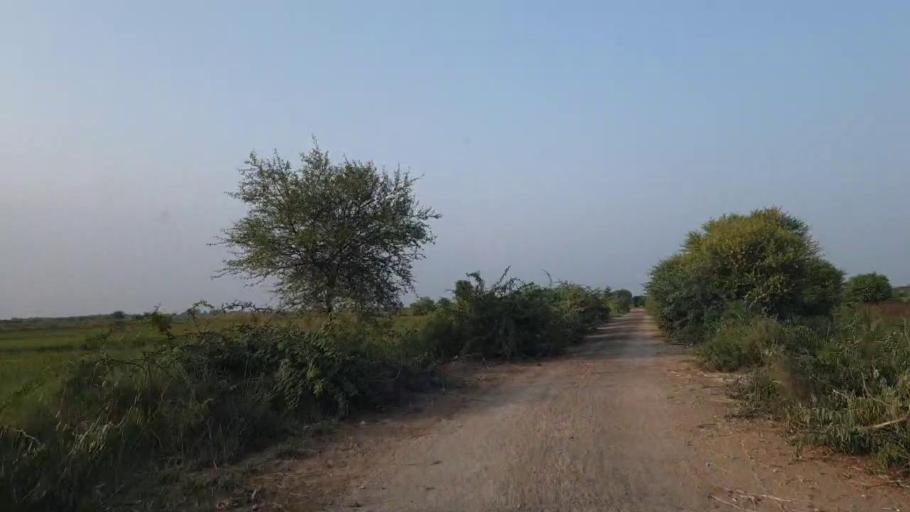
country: PK
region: Sindh
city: Rajo Khanani
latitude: 25.0353
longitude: 68.9634
